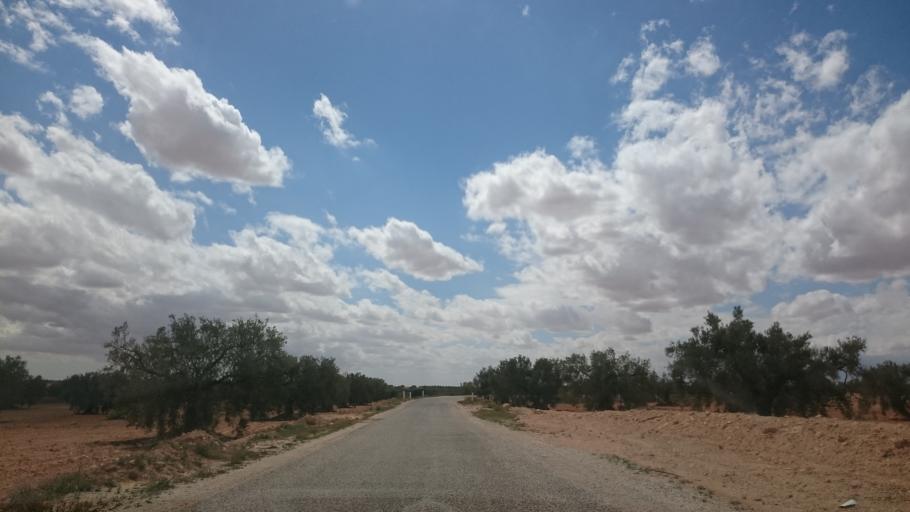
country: TN
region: Safaqis
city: Bi'r `Ali Bin Khalifah
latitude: 34.8162
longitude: 10.2924
